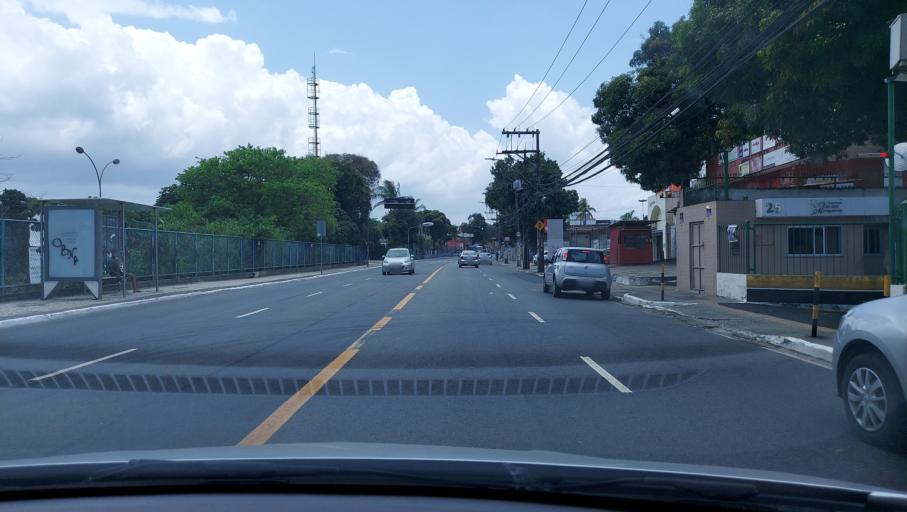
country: BR
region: Bahia
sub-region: Salvador
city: Salvador
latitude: -12.9638
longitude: -38.4721
